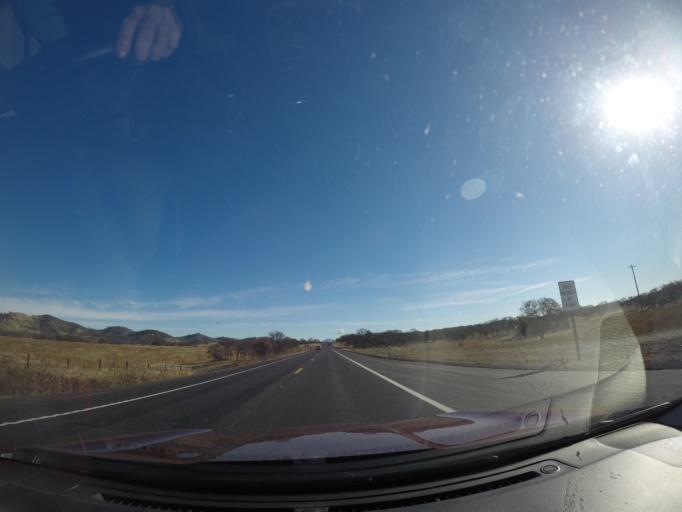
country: US
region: California
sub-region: Tuolumne County
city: Jamestown
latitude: 37.8422
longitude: -120.5243
